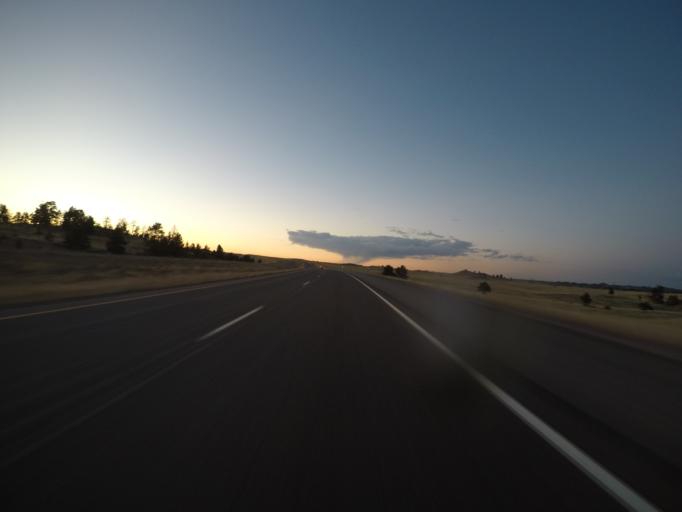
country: US
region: Wyoming
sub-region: Albany County
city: Laramie
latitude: 41.0130
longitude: -105.4195
